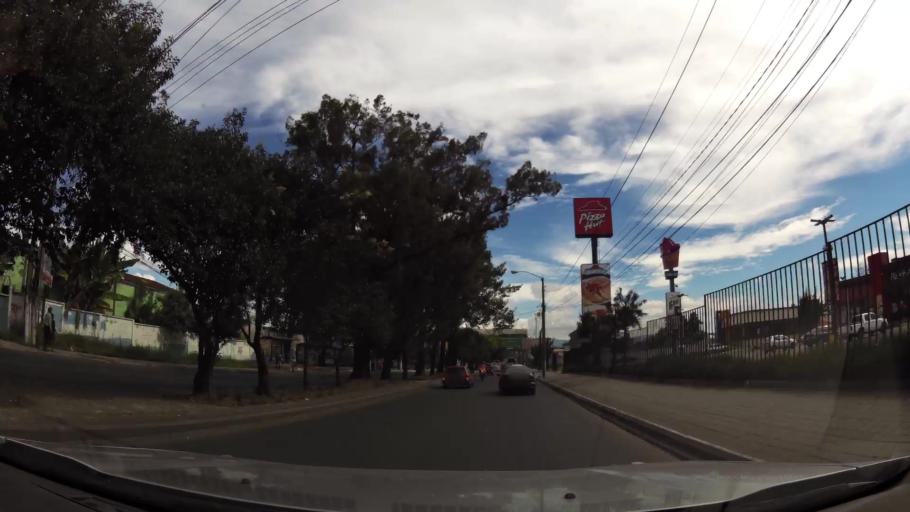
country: GT
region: Guatemala
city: Mixco
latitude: 14.6452
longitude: -90.5766
